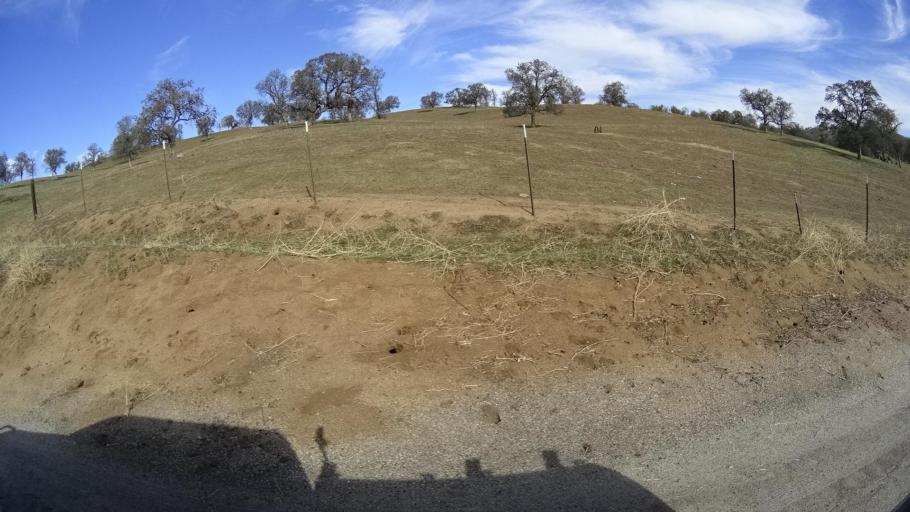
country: US
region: California
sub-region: Kern County
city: Oildale
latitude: 35.6151
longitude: -118.8431
